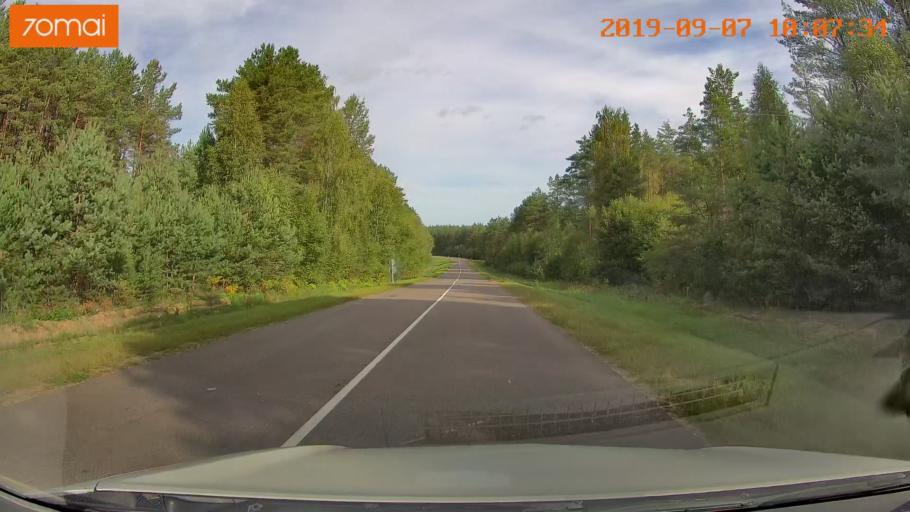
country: BY
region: Grodnenskaya
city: Voranava
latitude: 54.0773
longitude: 25.3961
